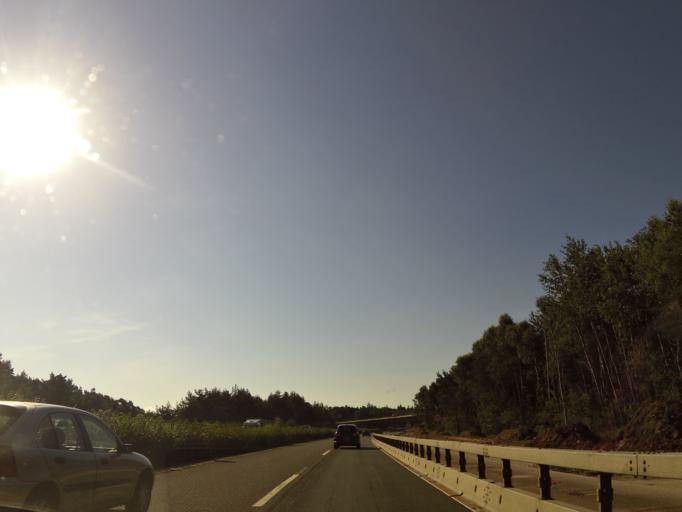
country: DE
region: Bavaria
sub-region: Regierungsbezirk Mittelfranken
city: Rothenbach an der Pegnitz
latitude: 49.4631
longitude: 11.2321
